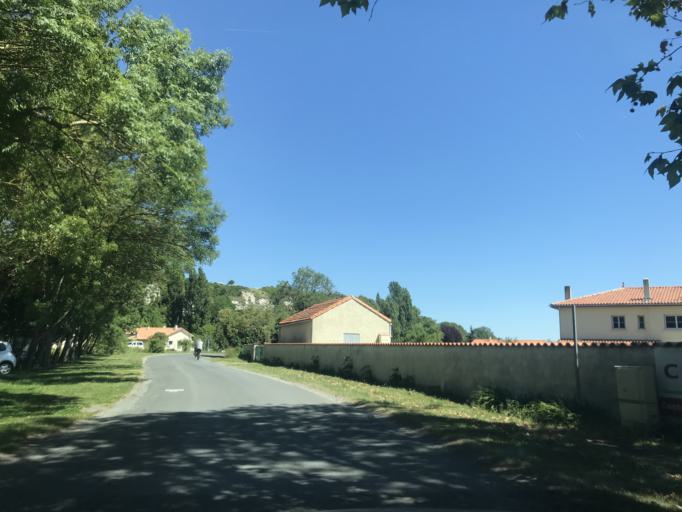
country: FR
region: Poitou-Charentes
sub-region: Departement de la Charente-Maritime
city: Mortagne-sur-Gironde
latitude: 45.4766
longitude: -0.7918
